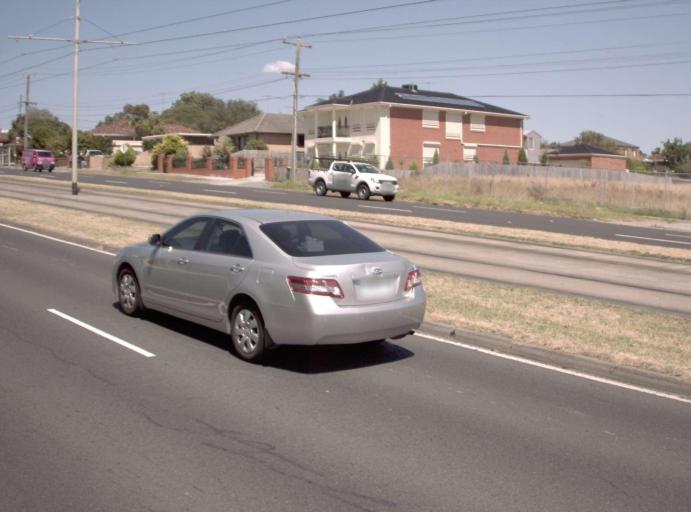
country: AU
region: Victoria
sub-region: Whitehorse
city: Burwood
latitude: -37.8508
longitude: 145.1229
